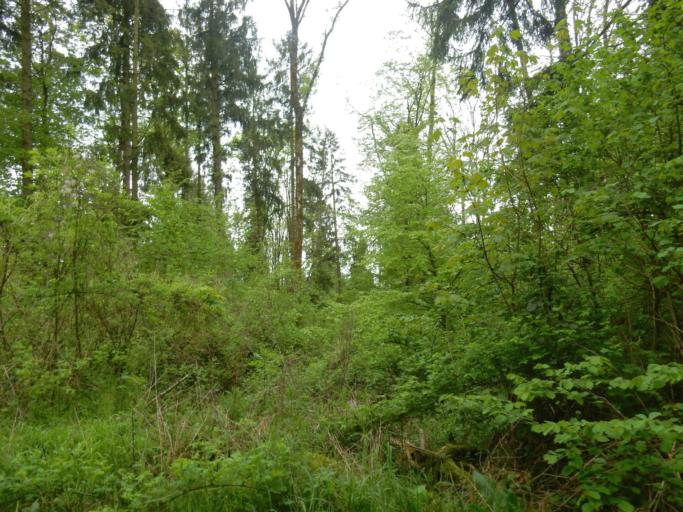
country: FR
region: Lorraine
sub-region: Departement de la Meuse
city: Verdun
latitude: 49.2160
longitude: 5.4454
